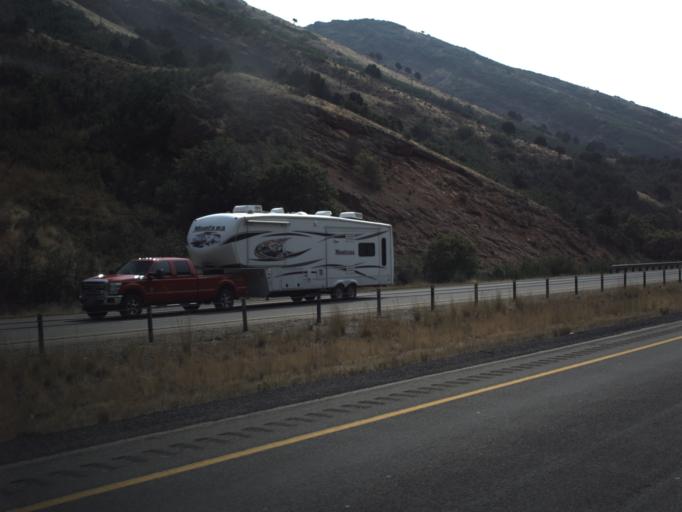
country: US
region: Utah
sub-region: Summit County
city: Coalville
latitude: 41.0064
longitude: -111.3823
